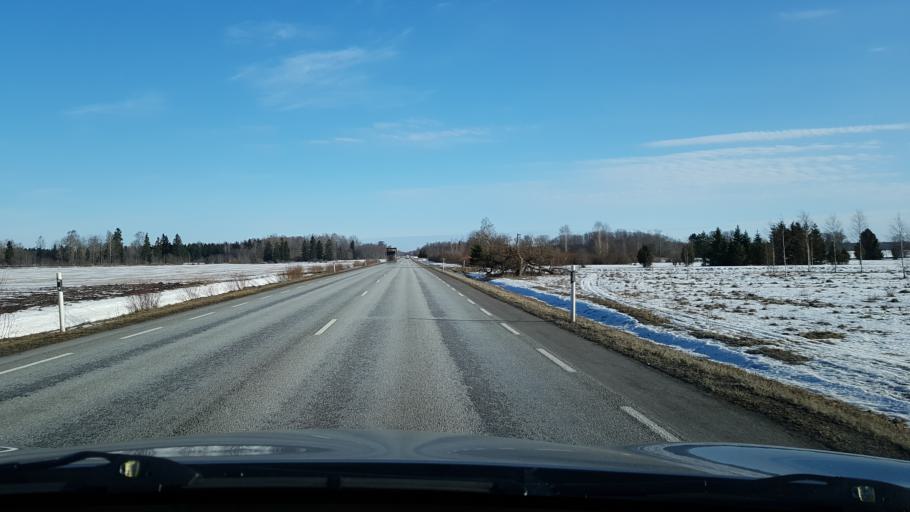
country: EE
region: Viljandimaa
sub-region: Vohma linn
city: Vohma
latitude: 58.6853
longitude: 25.6910
